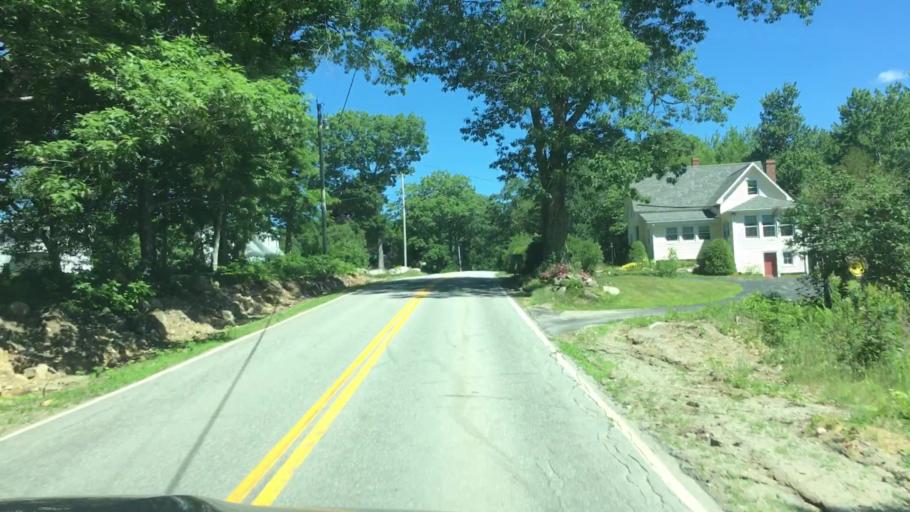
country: US
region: Maine
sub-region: Hancock County
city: Penobscot
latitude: 44.4317
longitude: -68.7138
